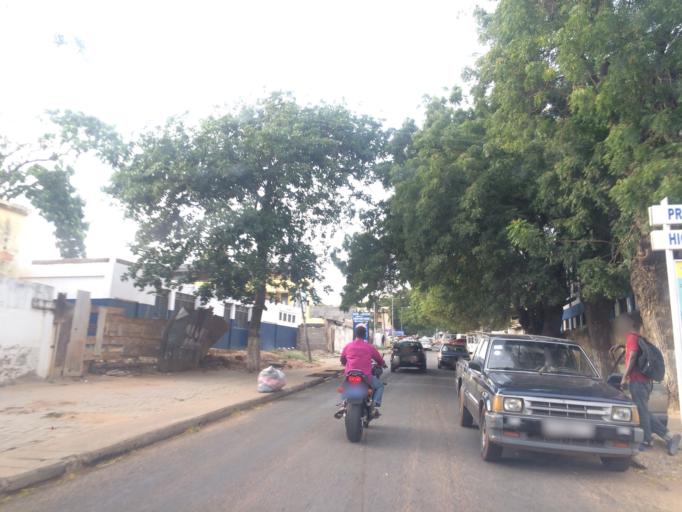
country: GH
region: Greater Accra
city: Accra
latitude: 5.5549
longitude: -0.1851
